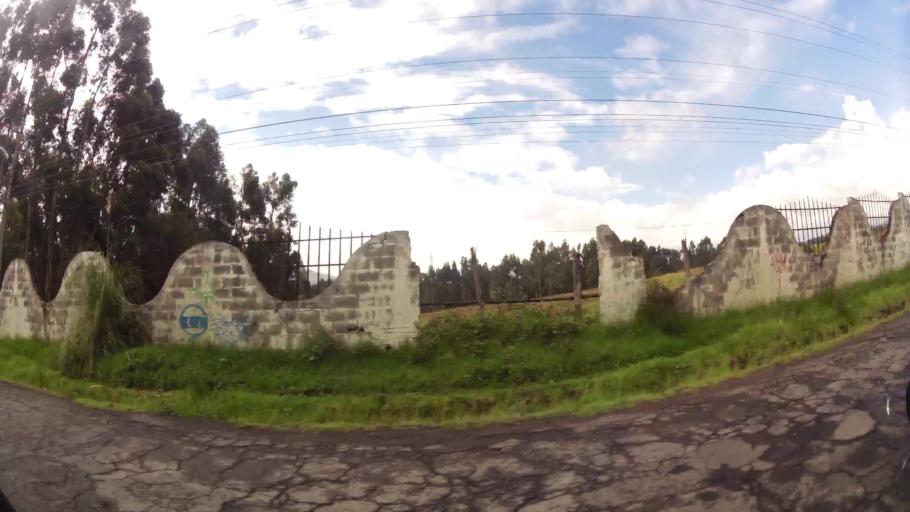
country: EC
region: Pichincha
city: Sangolqui
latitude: -0.3164
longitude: -78.4039
